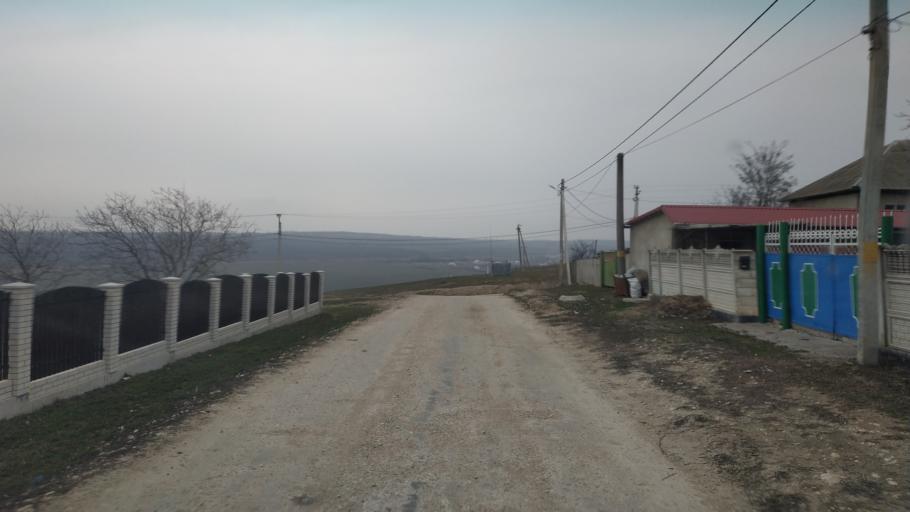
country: MD
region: Chisinau
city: Singera
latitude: 46.8258
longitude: 28.9627
